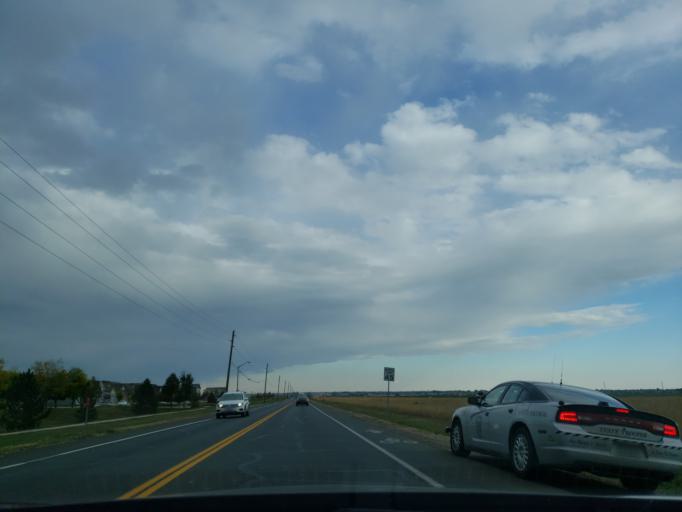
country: US
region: Colorado
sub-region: Larimer County
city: Fort Collins
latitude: 40.6102
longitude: -105.0383
